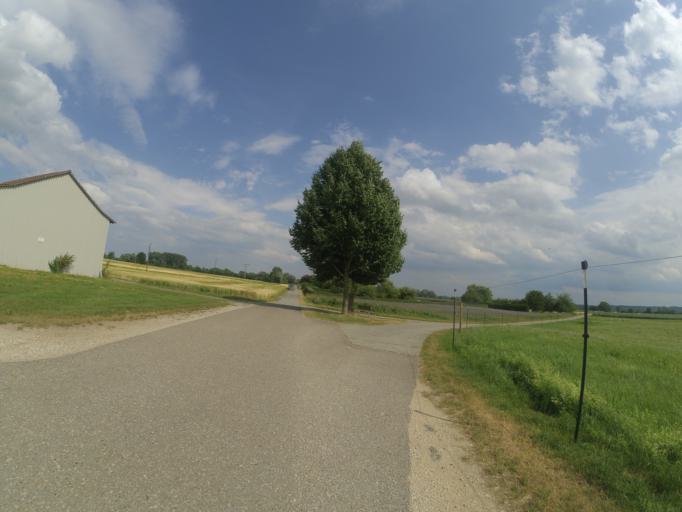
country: DE
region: Baden-Wuerttemberg
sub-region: Tuebingen Region
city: Opfingen
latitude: 48.2814
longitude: 9.8077
